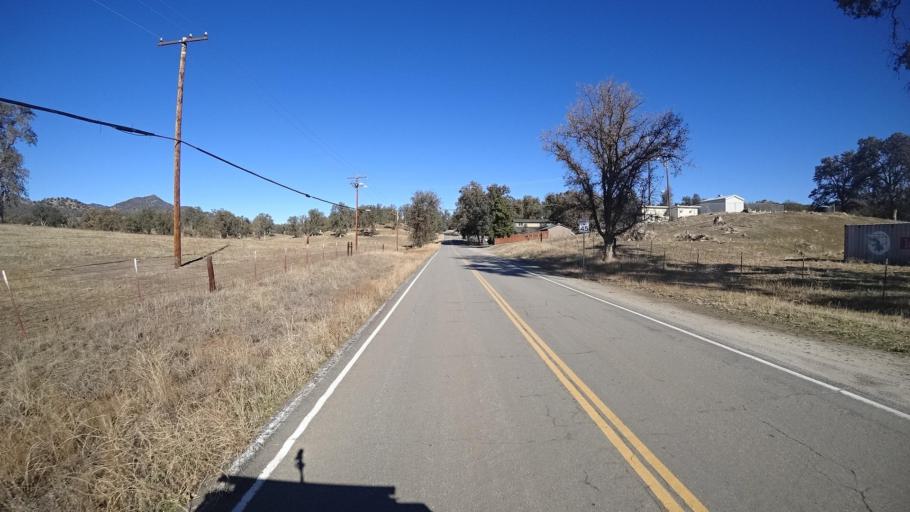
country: US
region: California
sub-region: Kern County
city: Alta Sierra
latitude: 35.7262
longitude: -118.7221
